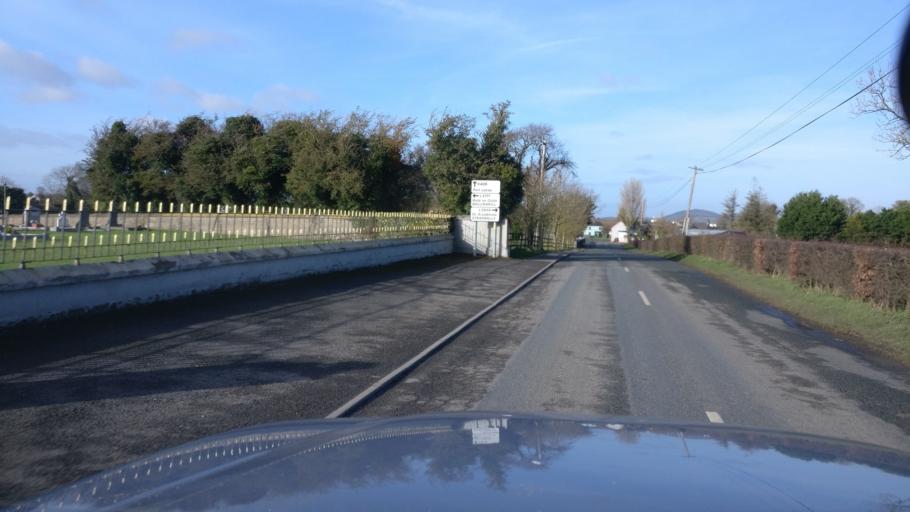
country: IE
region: Leinster
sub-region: Laois
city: Stradbally
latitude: 52.9583
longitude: -7.2002
